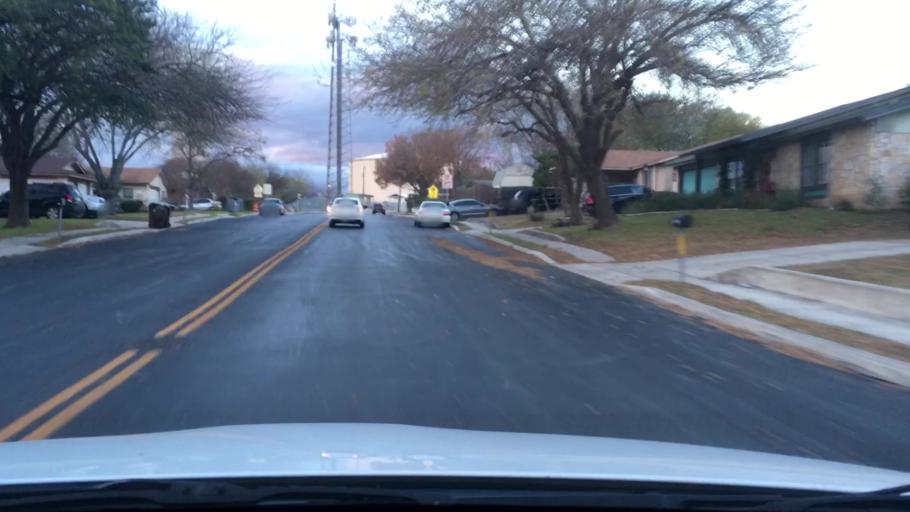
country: US
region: Texas
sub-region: Bexar County
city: Windcrest
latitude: 29.5279
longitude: -98.3533
